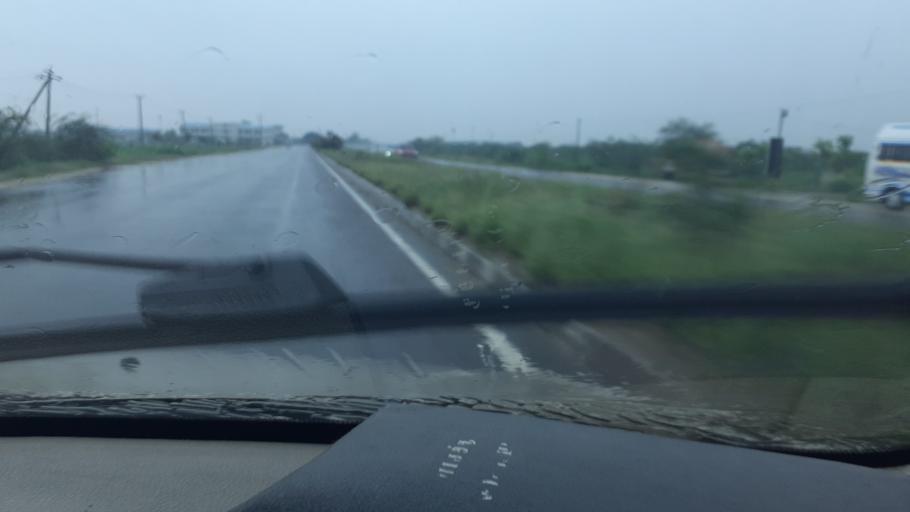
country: IN
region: Tamil Nadu
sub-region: Virudhunagar
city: Sattur
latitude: 9.4047
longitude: 77.9166
